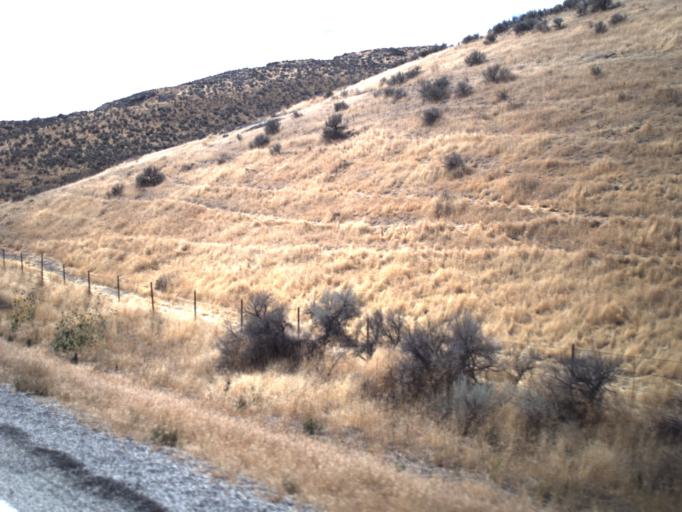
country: US
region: Utah
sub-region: Box Elder County
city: Tremonton
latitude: 41.6828
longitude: -112.4444
